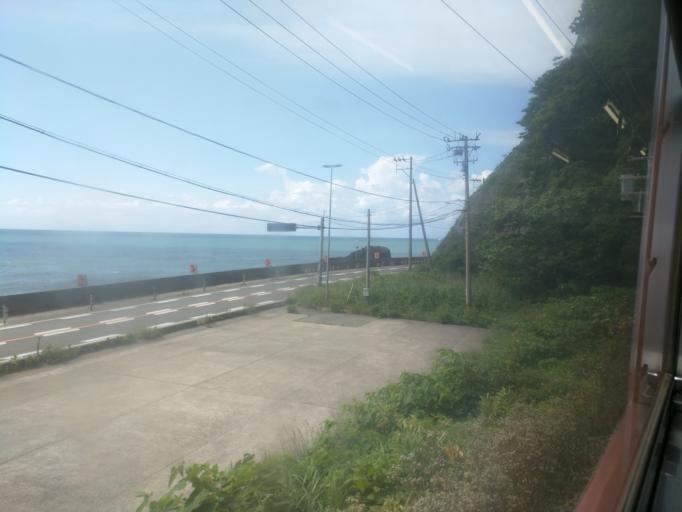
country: JP
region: Niigata
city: Murakami
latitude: 38.5300
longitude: 139.5422
